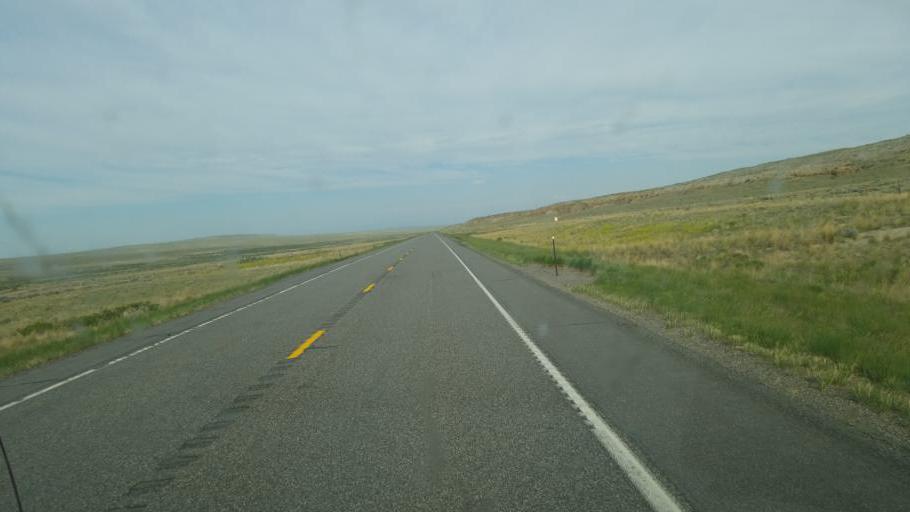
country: US
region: Wyoming
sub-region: Fremont County
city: Riverton
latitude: 43.2221
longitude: -107.9818
